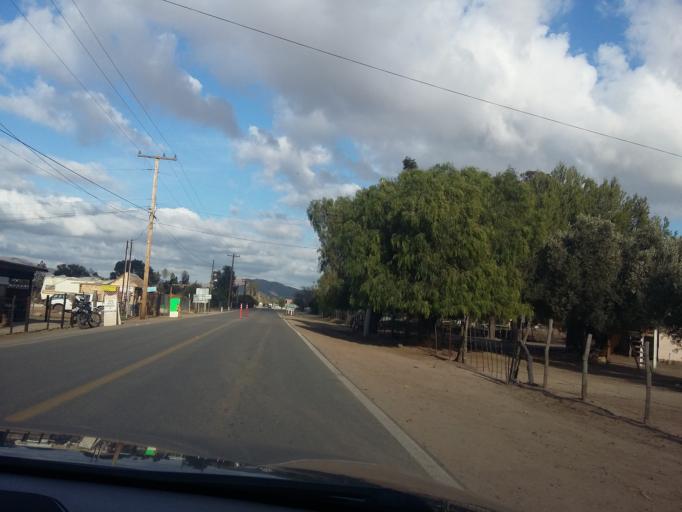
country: MX
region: Baja California
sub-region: Ensenada
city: Rancho Verde
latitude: 32.0694
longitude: -116.6360
